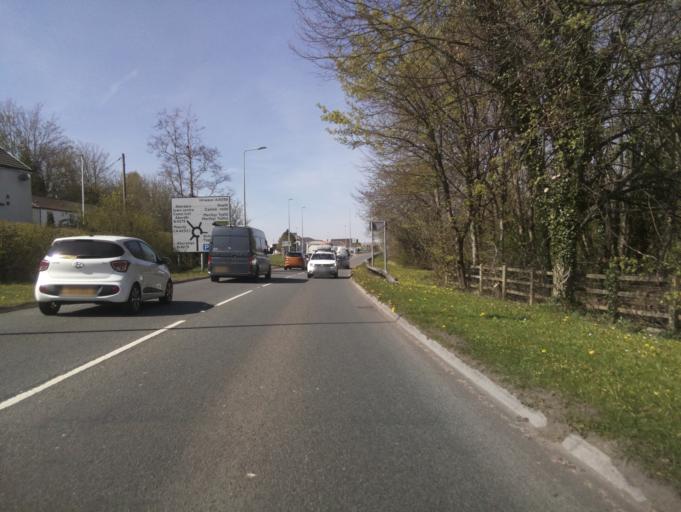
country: GB
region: Wales
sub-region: Rhondda Cynon Taf
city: Aberdare
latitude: 51.7098
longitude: -3.4389
